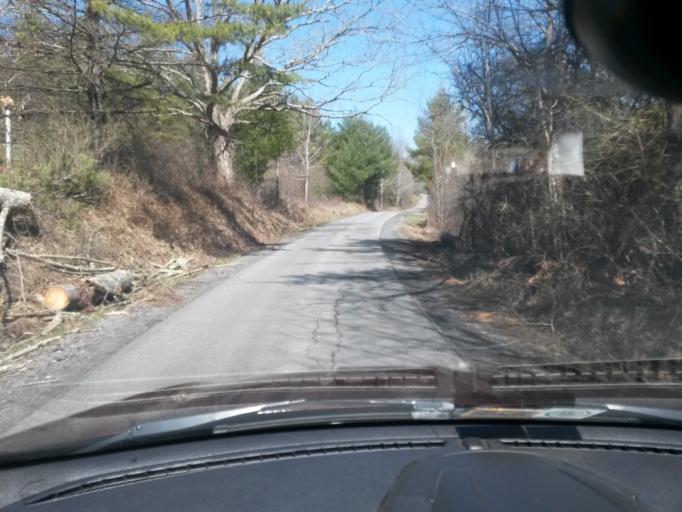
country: US
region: West Virginia
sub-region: Greenbrier County
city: White Sulphur Springs
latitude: 37.6569
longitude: -80.3218
